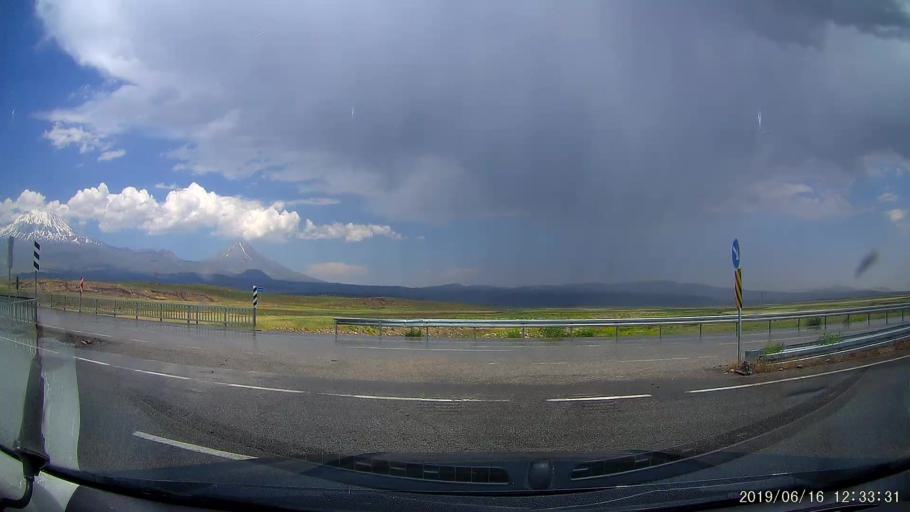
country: TR
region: Agri
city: Dogubayazit
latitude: 39.4671
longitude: 44.2612
